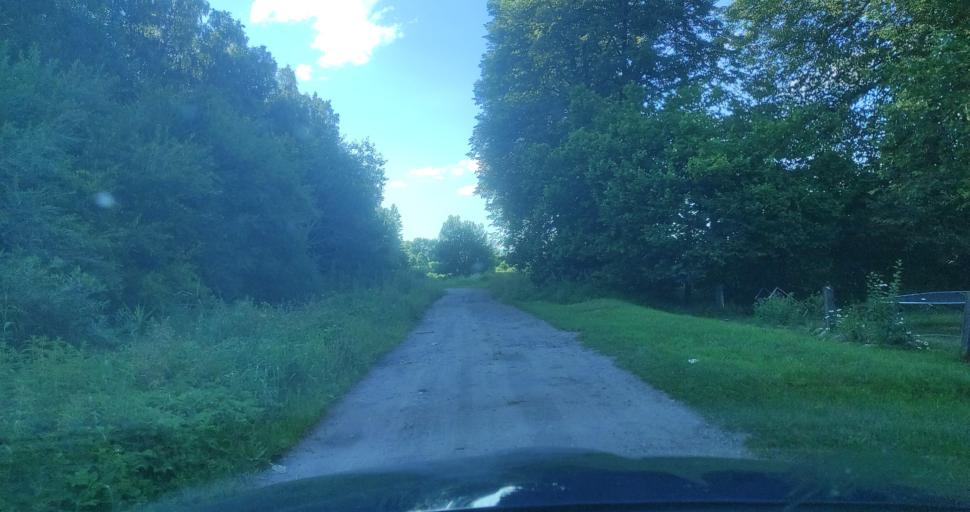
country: LV
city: Tireli
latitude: 56.7026
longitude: 23.4618
